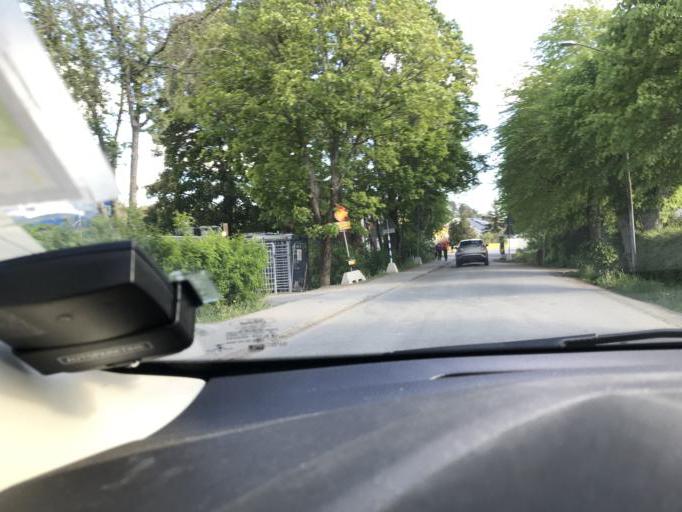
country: SE
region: Stockholm
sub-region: Botkyrka Kommun
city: Tumba
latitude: 59.1955
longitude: 17.8251
